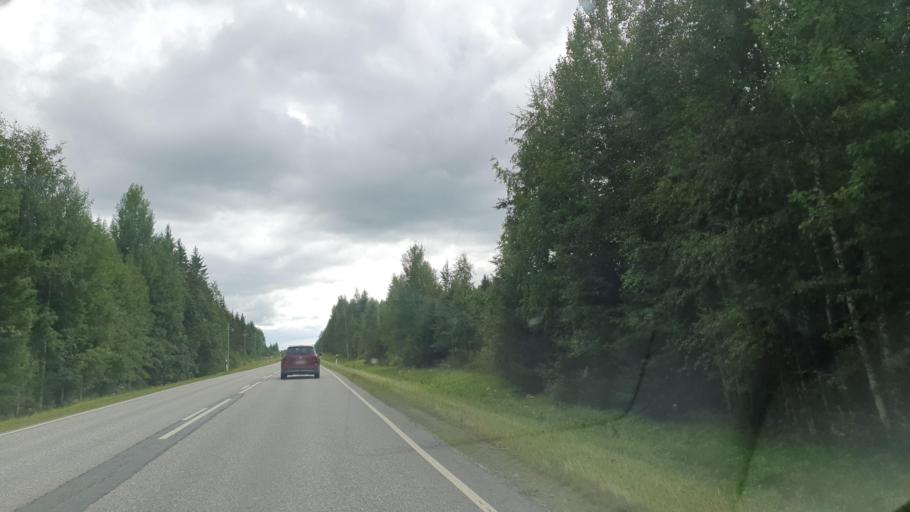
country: FI
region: Northern Savo
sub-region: Ylae-Savo
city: Sonkajaervi
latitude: 63.7178
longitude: 27.3654
